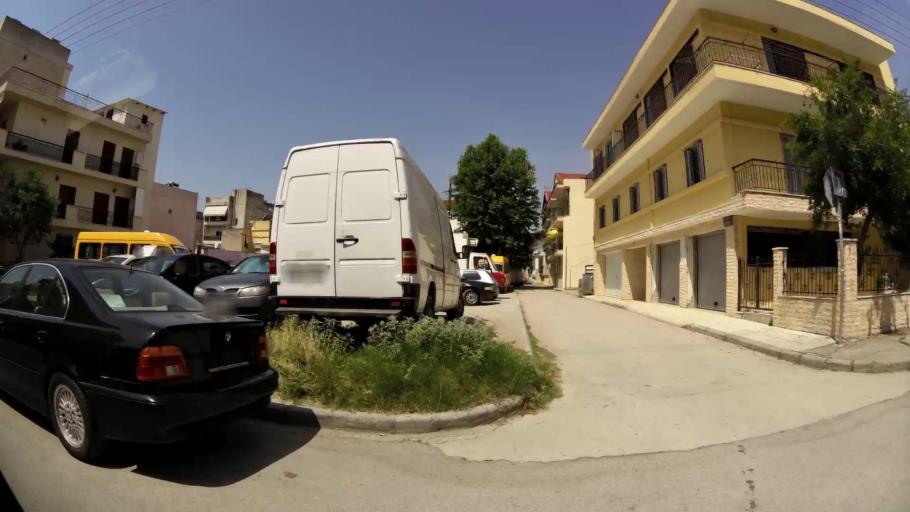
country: GR
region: Central Macedonia
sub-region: Nomos Thessalonikis
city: Evosmos
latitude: 40.6678
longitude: 22.9179
